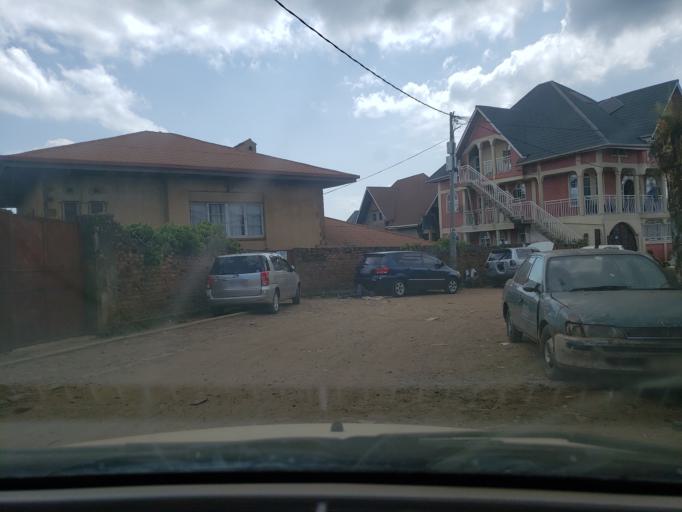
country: RW
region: Western Province
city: Cyangugu
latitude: -2.5003
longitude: 28.8814
